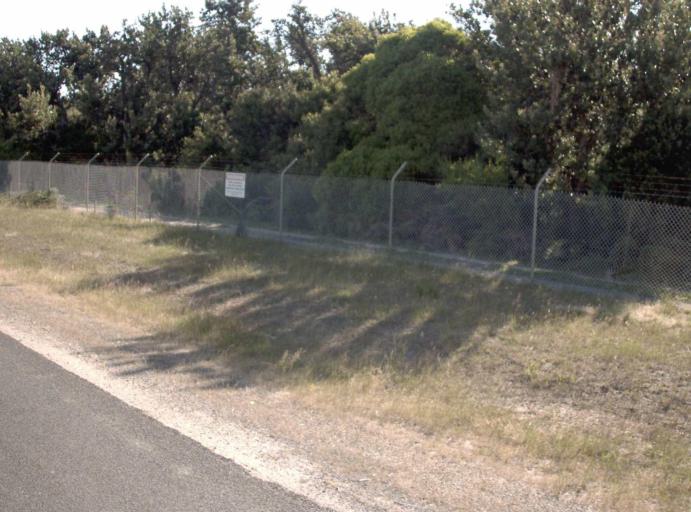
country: AU
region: Victoria
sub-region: Latrobe
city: Morwell
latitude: -38.7132
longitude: 146.3962
